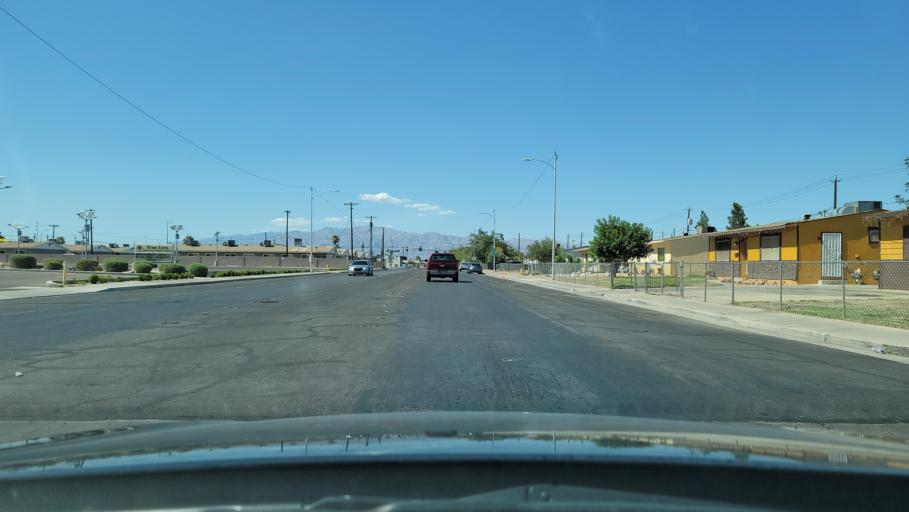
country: US
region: Nevada
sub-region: Clark County
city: Las Vegas
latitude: 36.1937
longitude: -115.1518
